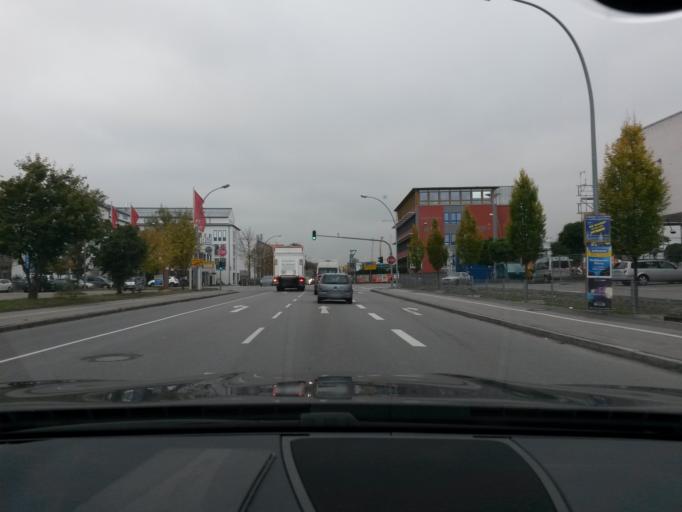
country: DE
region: Bavaria
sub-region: Lower Bavaria
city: Ergolding
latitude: 48.5579
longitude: 12.1559
